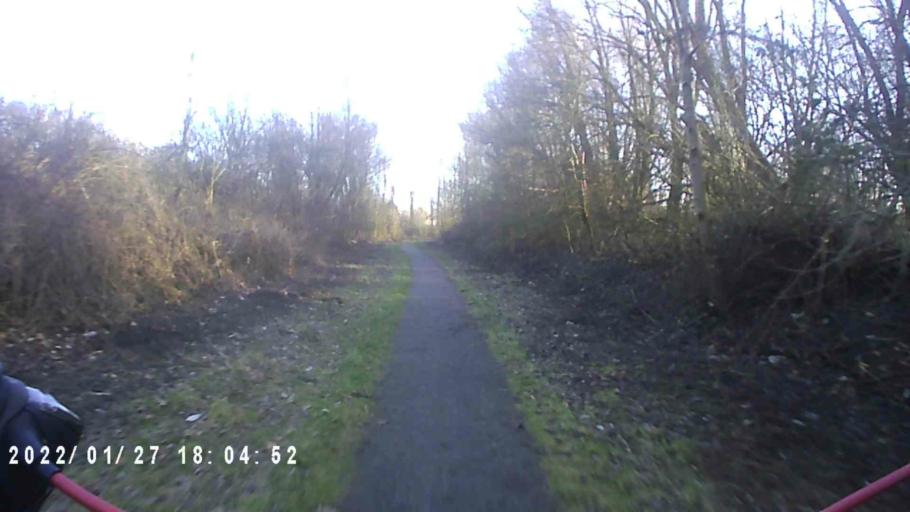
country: NL
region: Friesland
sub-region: Gemeente Dongeradeel
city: Anjum
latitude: 53.4066
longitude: 6.2163
